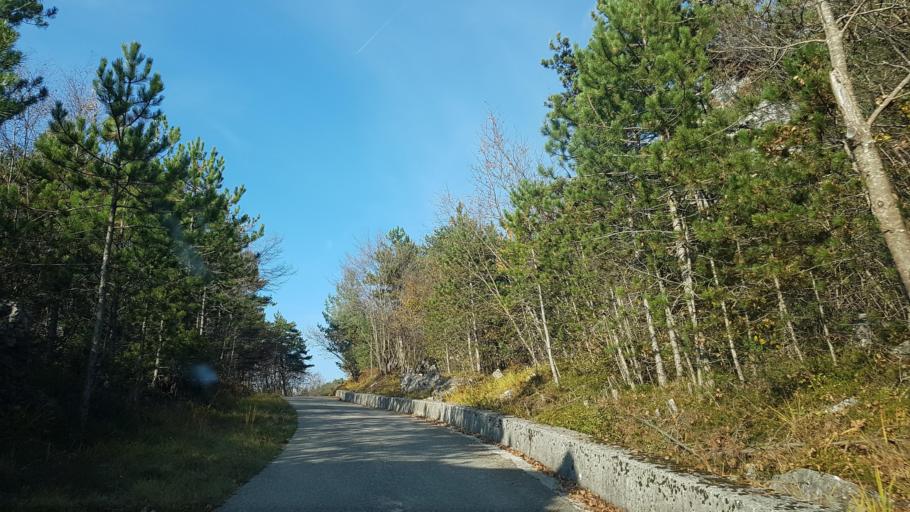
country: IT
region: Friuli Venezia Giulia
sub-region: Provincia di Udine
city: Moggio Udinese
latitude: 46.4416
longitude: 13.2041
